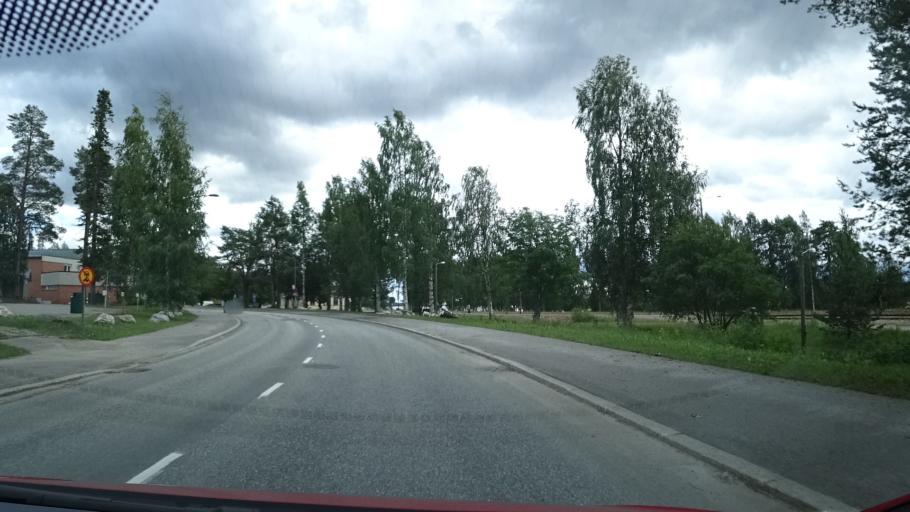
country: FI
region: North Karelia
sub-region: Pielisen Karjala
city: Nurmes
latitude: 63.5421
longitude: 29.1356
